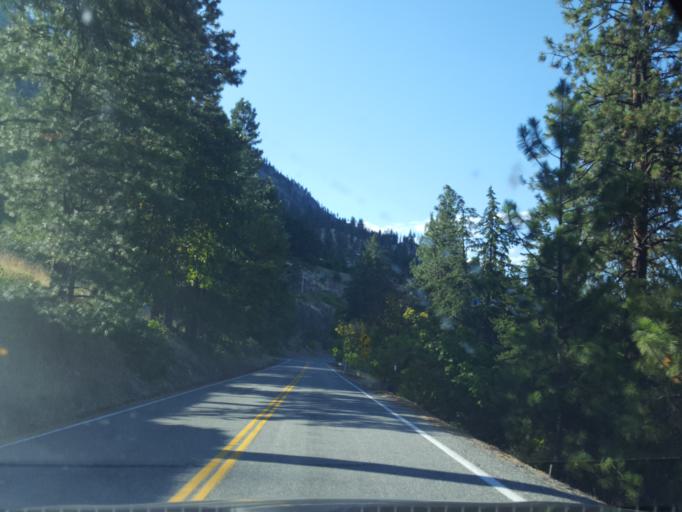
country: US
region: Washington
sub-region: Chelan County
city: Granite Falls
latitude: 47.9424
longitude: -120.2119
